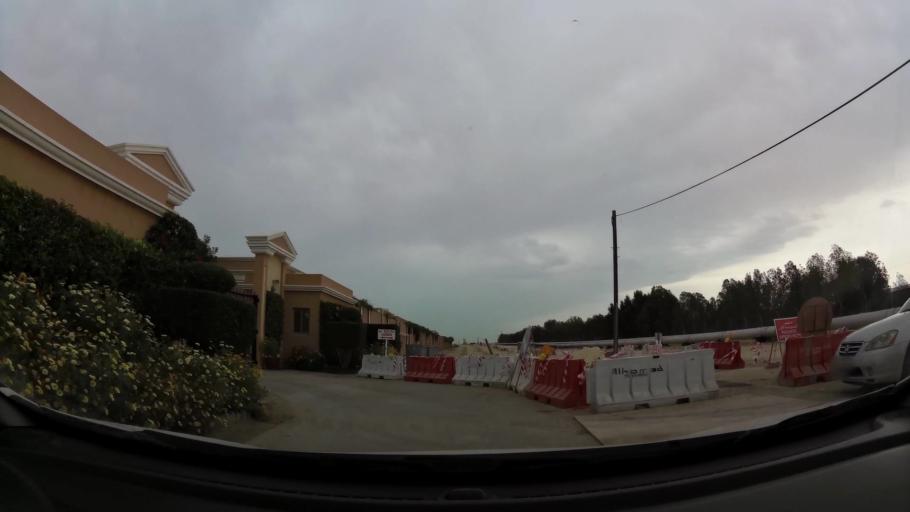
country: BH
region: Central Governorate
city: Madinat Hamad
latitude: 26.1438
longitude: 50.4764
